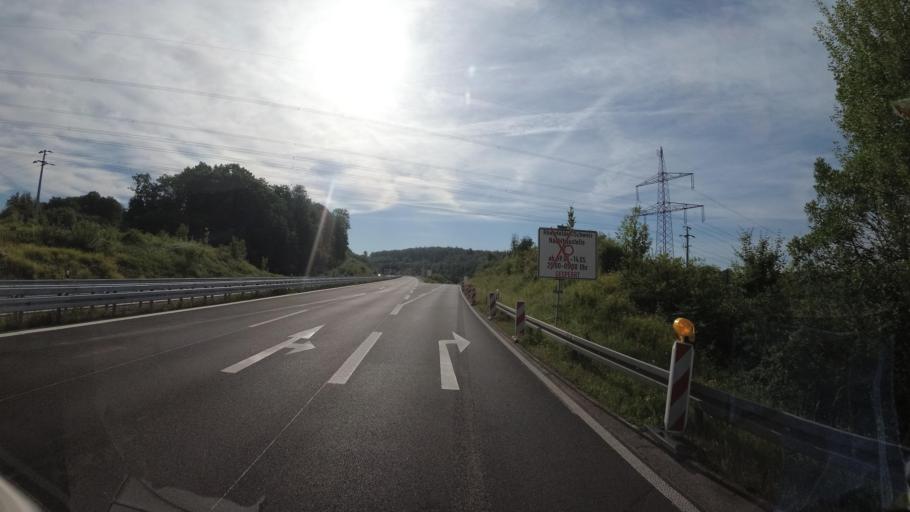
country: DE
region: Baden-Wuerttemberg
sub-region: Freiburg Region
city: Rheinfelden (Baden)
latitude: 47.5867
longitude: 7.7523
